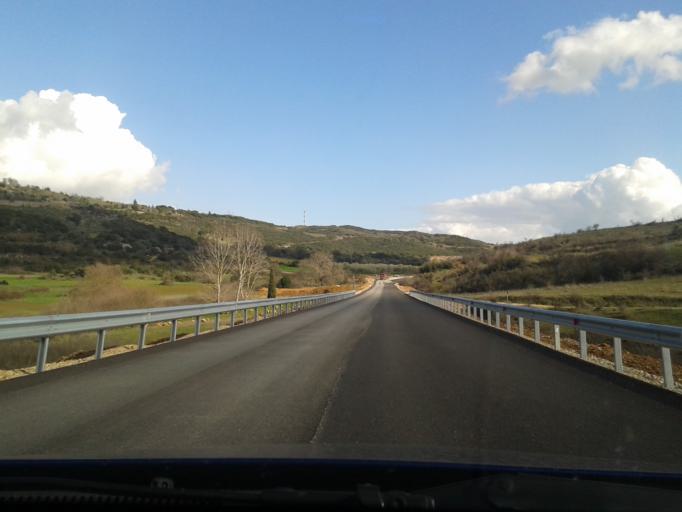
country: GR
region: West Greece
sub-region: Nomos Aitolias kai Akarnanias
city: Fitiai
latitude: 38.6873
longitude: 21.1737
